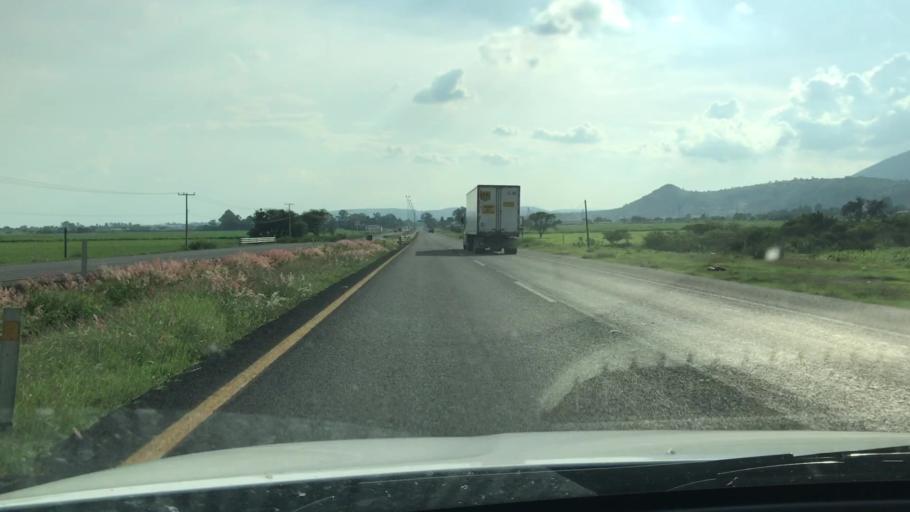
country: MX
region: Guanajuato
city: Penjamo
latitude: 20.4391
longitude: -101.6817
